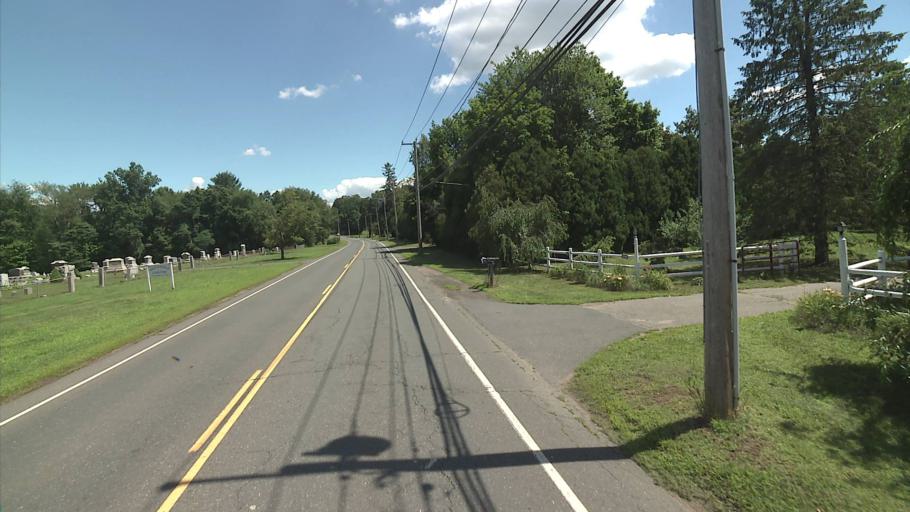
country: US
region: Connecticut
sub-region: Hartford County
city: Suffield Depot
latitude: 41.9882
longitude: -72.6932
